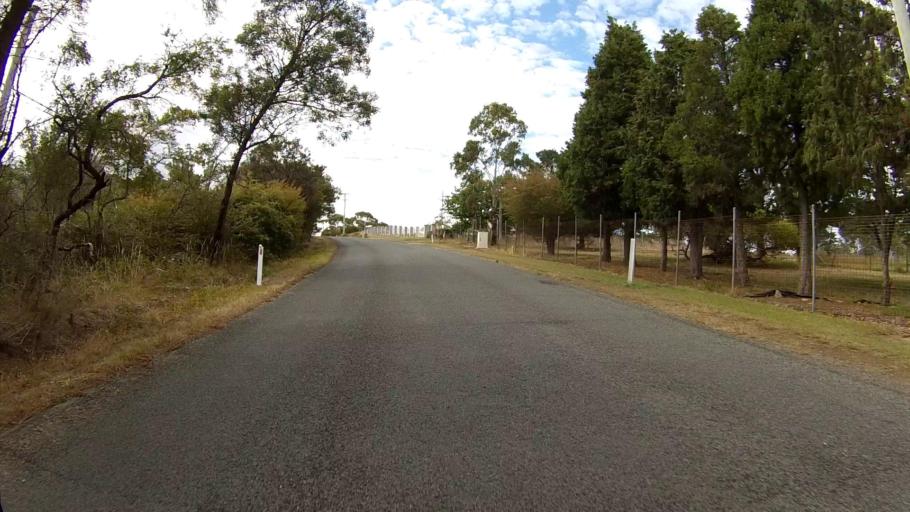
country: AU
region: Tasmania
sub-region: Glenorchy
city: Goodwood
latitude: -42.7994
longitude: 147.2896
